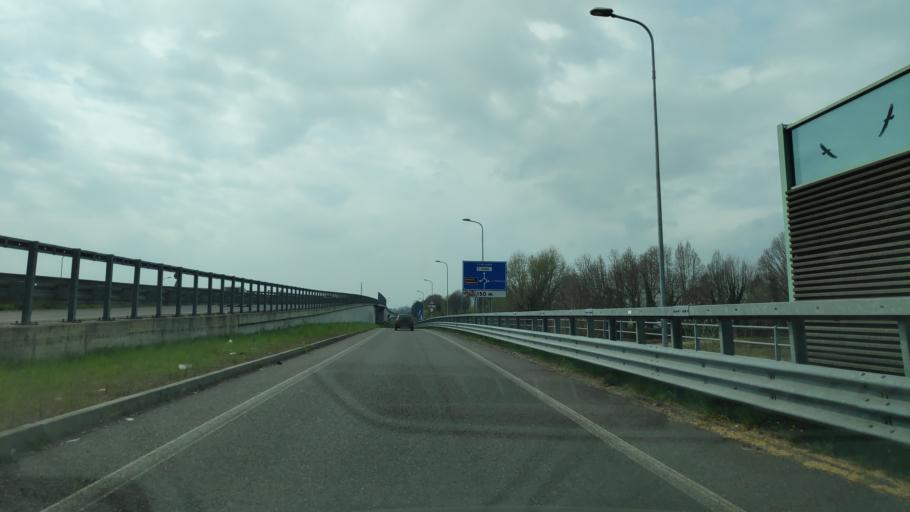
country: IT
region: Lombardy
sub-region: Citta metropolitana di Milano
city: Lucino-Rodano
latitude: 45.4827
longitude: 9.3475
